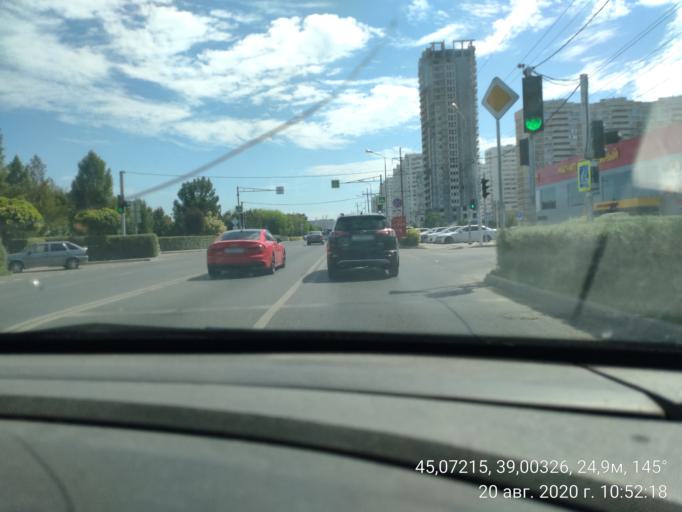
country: RU
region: Krasnodarskiy
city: Krasnodar
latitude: 45.0721
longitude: 39.0032
